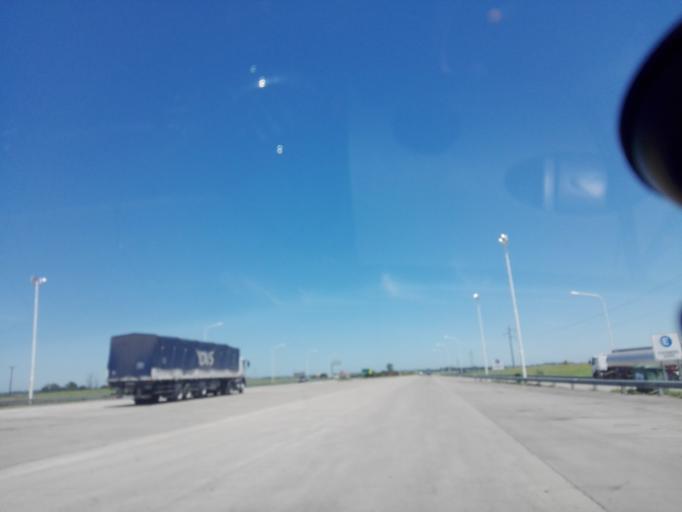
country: AR
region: Santa Fe
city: Carcarana
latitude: -32.8760
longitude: -61.1707
